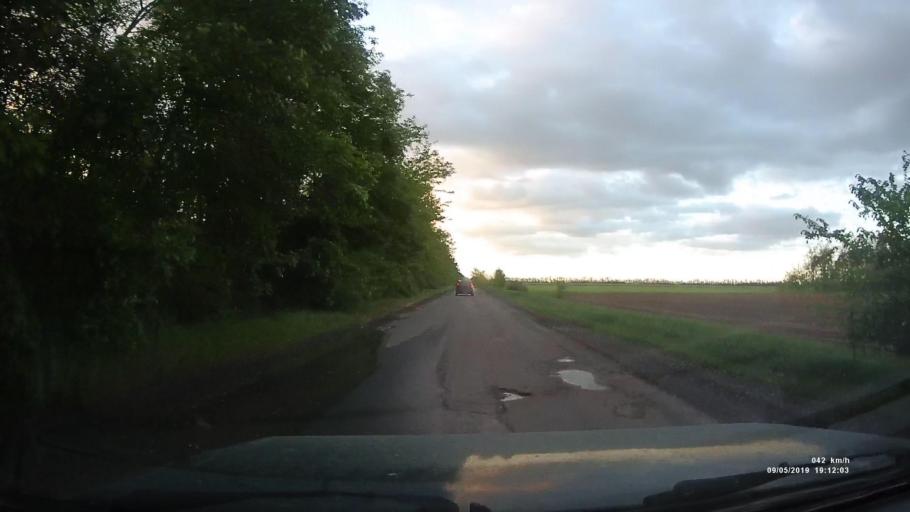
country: RU
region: Krasnodarskiy
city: Kanelovskaya
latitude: 46.7391
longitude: 39.2136
